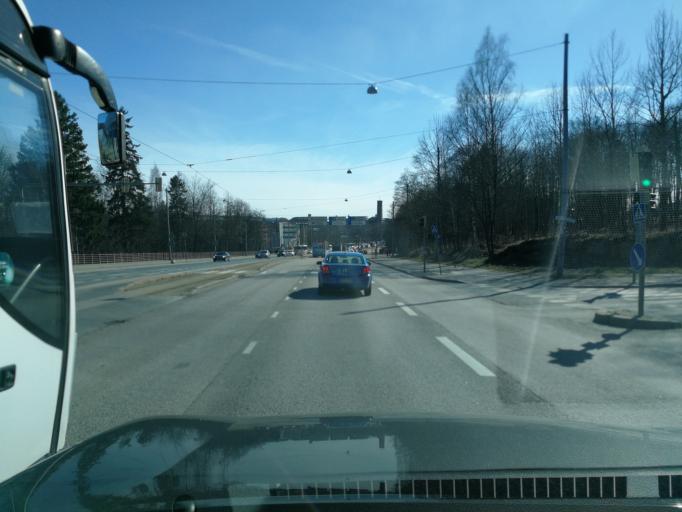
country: FI
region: Uusimaa
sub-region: Helsinki
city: Helsinki
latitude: 60.2054
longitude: 24.9668
